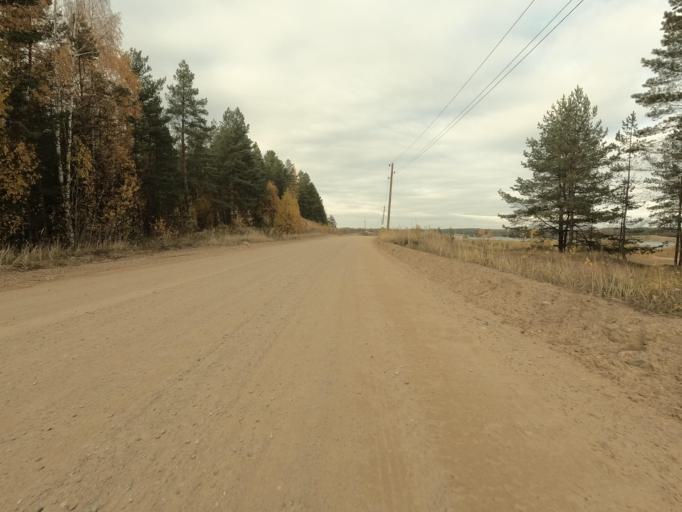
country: RU
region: Leningrad
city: Priladozhskiy
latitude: 59.6981
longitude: 31.3621
